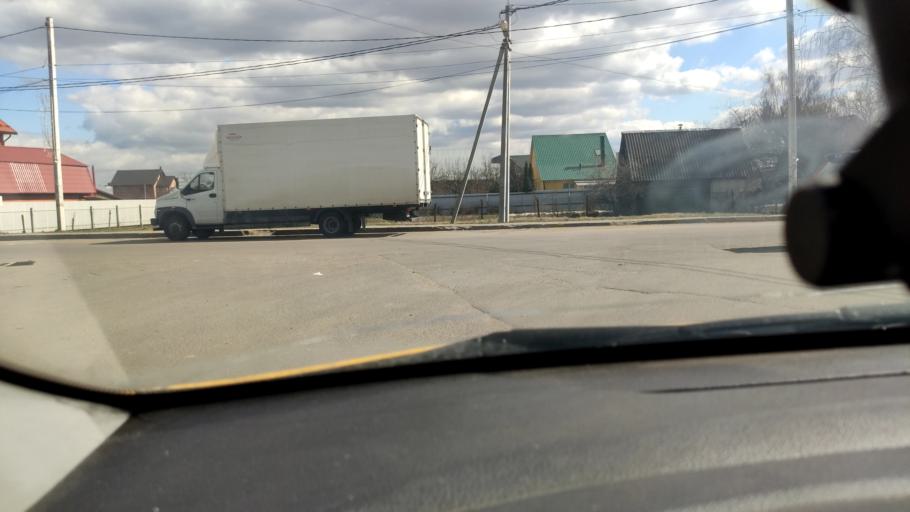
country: RU
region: Moskovskaya
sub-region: Leninskiy Rayon
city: Molokovo
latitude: 55.5626
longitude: 37.8619
